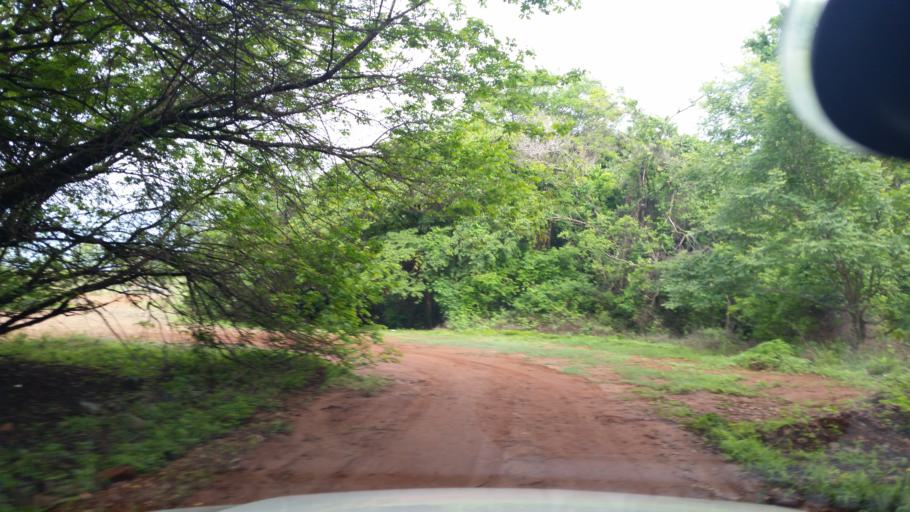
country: BR
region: Goias
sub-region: Porangatu
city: Porangatu
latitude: -13.9797
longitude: -49.2739
